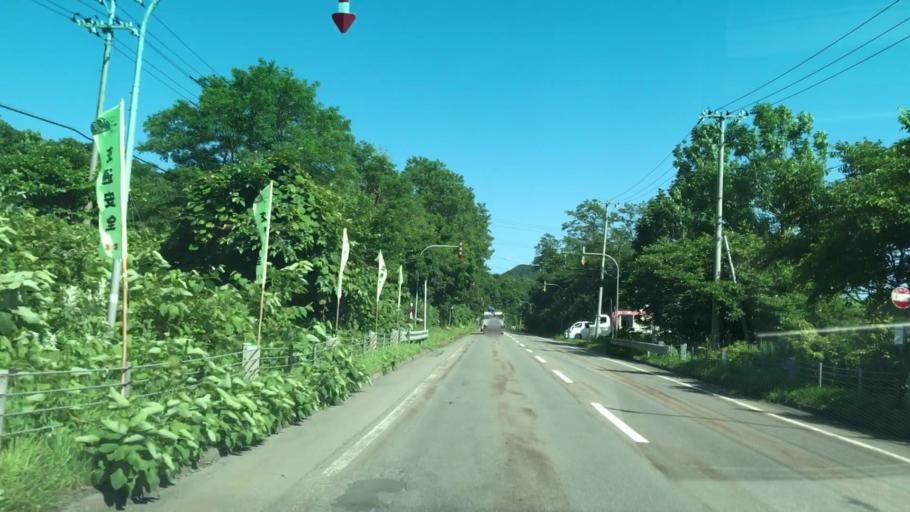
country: JP
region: Hokkaido
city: Iwanai
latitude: 43.0779
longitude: 140.4840
